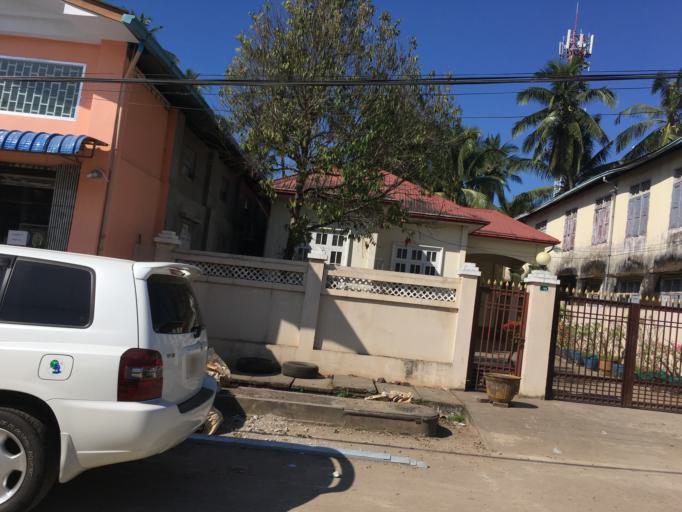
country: MM
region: Mon
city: Mawlamyine
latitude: 16.4938
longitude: 97.6330
